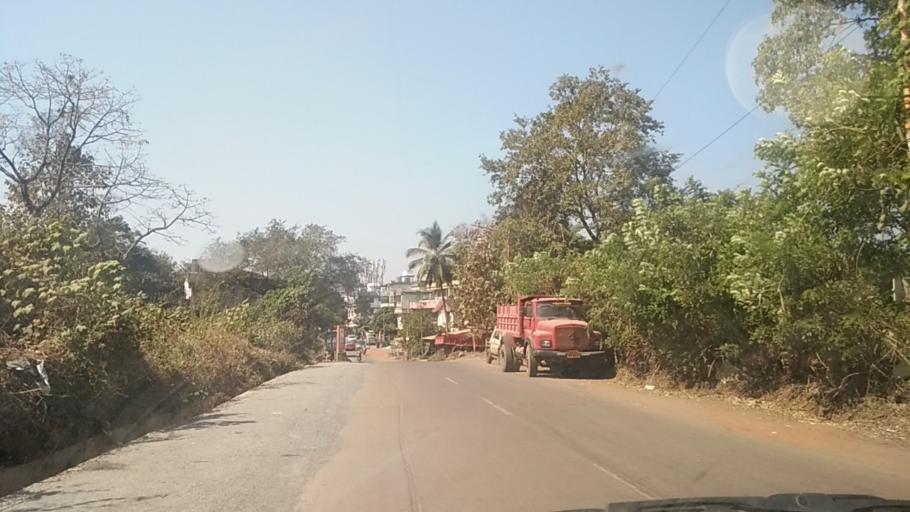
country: IN
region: Goa
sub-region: South Goa
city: Raia
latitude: 15.2996
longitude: 73.9660
